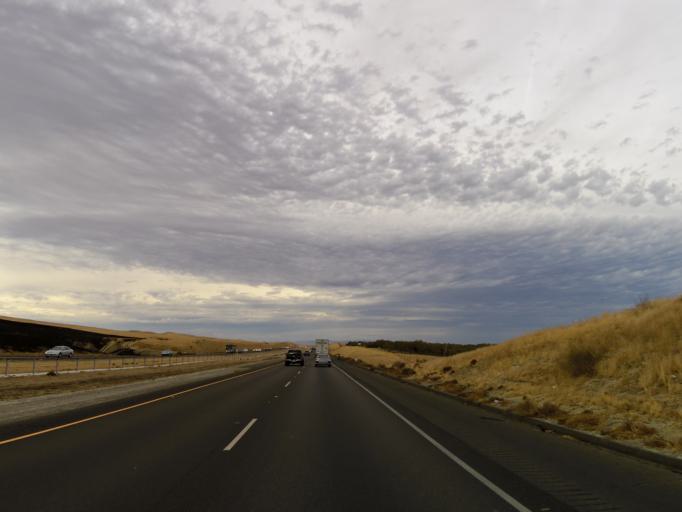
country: US
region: California
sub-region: Kings County
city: Kettleman City
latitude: 36.0370
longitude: -120.0340
